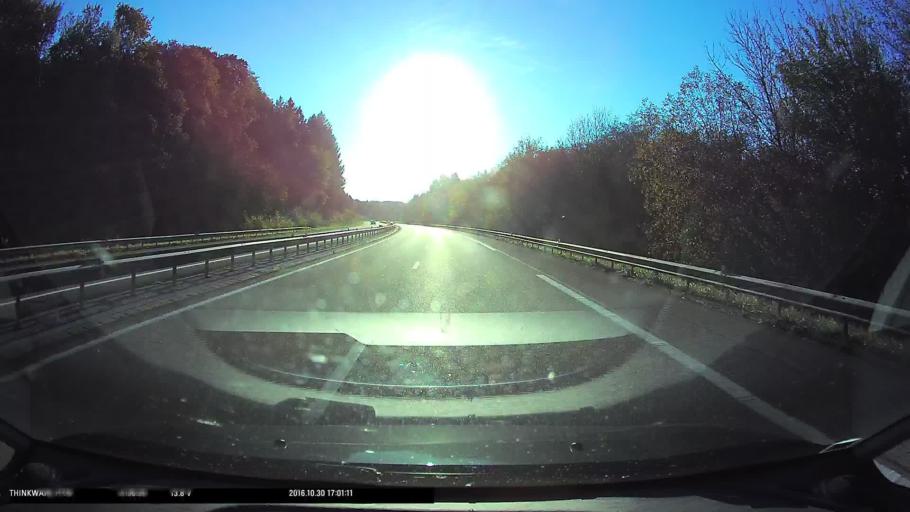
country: FR
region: Franche-Comte
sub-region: Departement du Jura
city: Orchamps
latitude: 47.1820
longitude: 5.6854
